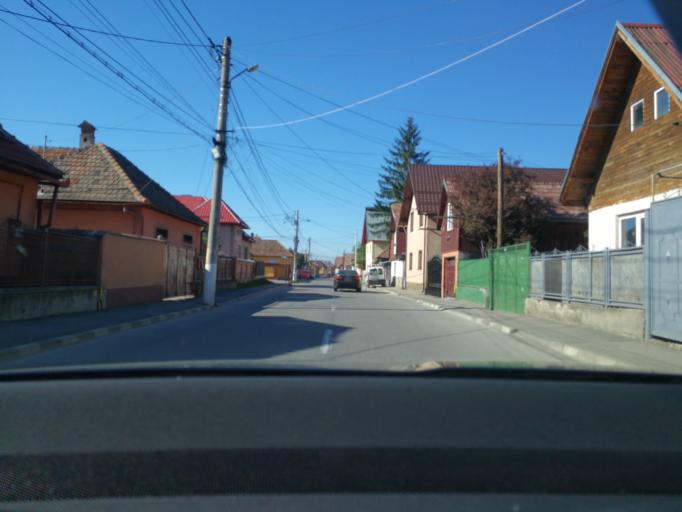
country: RO
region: Brasov
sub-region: Oras Rasnov
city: Rasnov
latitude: 45.5849
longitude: 25.4591
